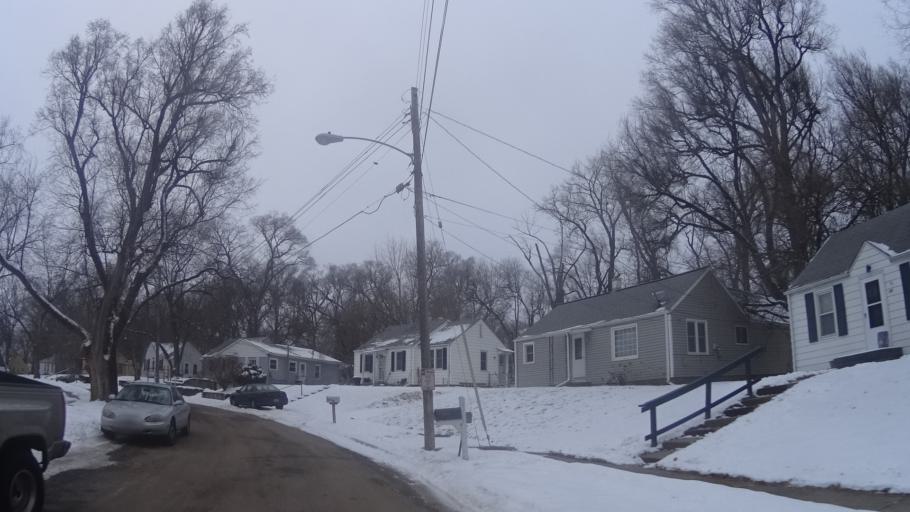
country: US
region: Nebraska
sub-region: Sarpy County
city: Offutt Air Force Base
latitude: 41.1369
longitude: -95.9222
